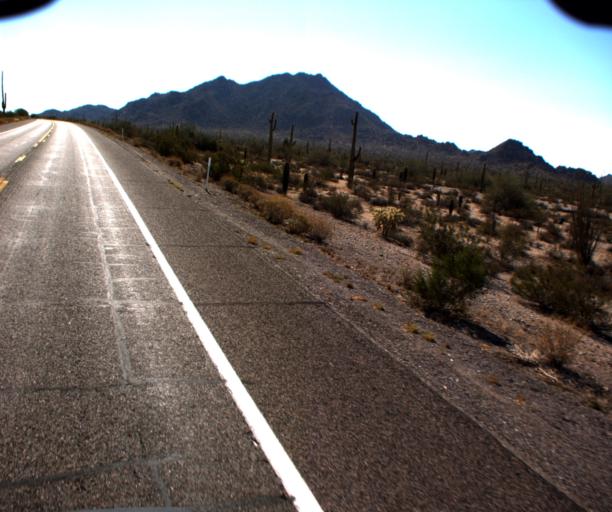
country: US
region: Arizona
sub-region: Pinal County
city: Sacaton
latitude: 33.0062
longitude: -111.7074
